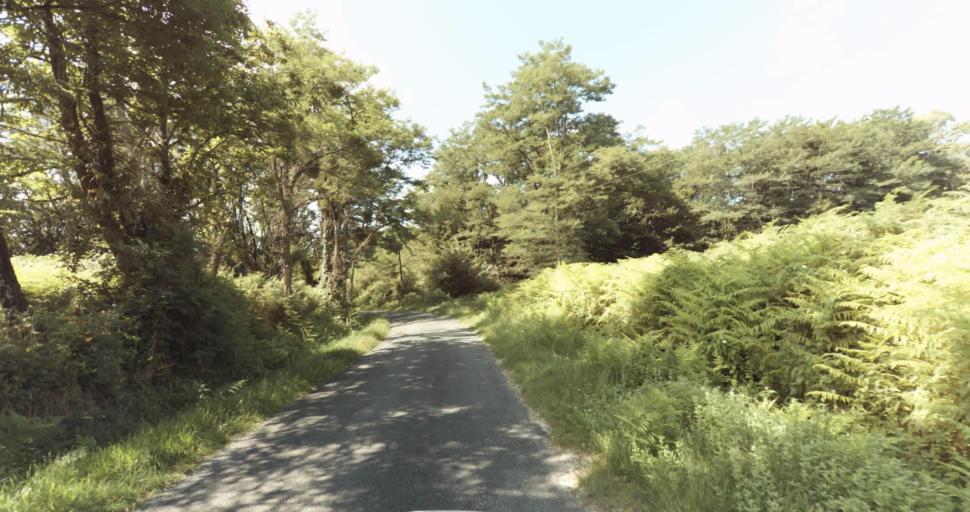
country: FR
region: Aquitaine
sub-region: Departement de la Gironde
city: Bazas
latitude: 44.4654
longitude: -0.2177
